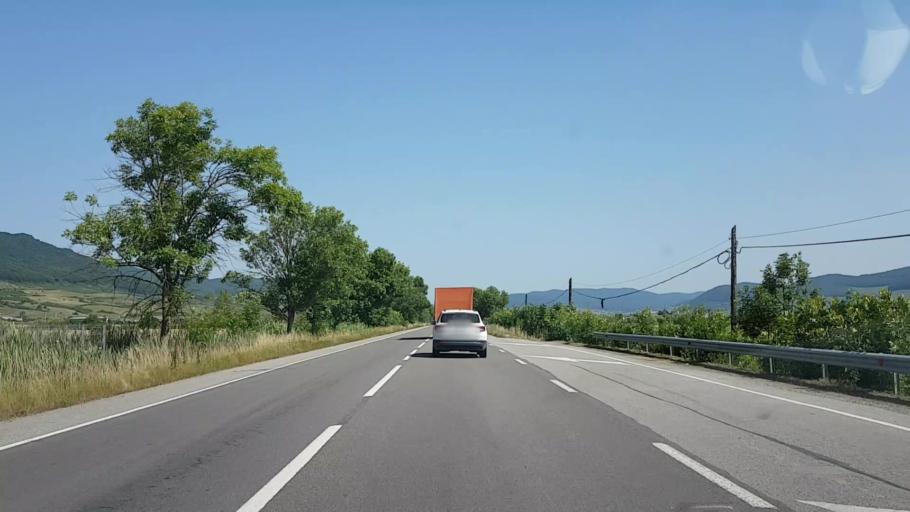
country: RO
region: Bistrita-Nasaud
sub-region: Comuna Sieu-Magherus
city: Sieu-Magherus
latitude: 47.1068
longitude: 24.3506
